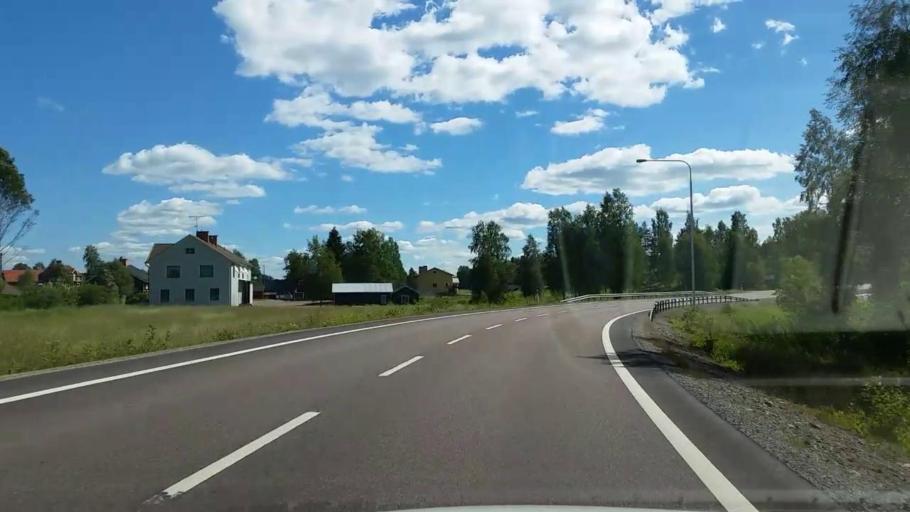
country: SE
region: Dalarna
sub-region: Faluns Kommun
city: Svardsjo
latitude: 60.7150
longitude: 15.7811
